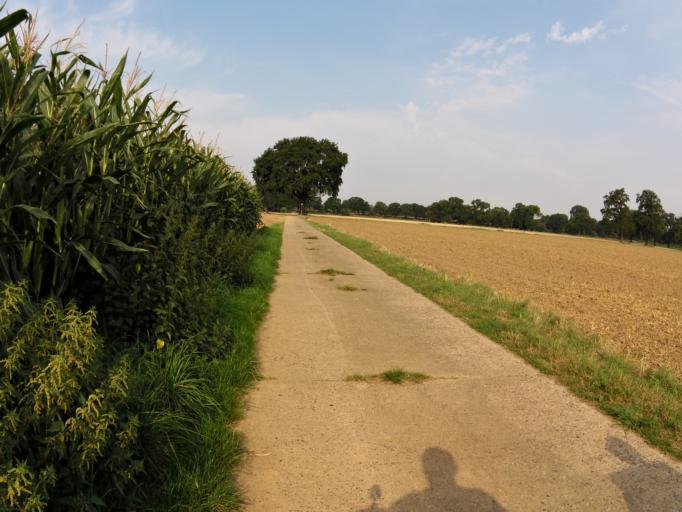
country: DE
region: Lower Saxony
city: Raddestorf
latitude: 52.4689
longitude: 9.0153
